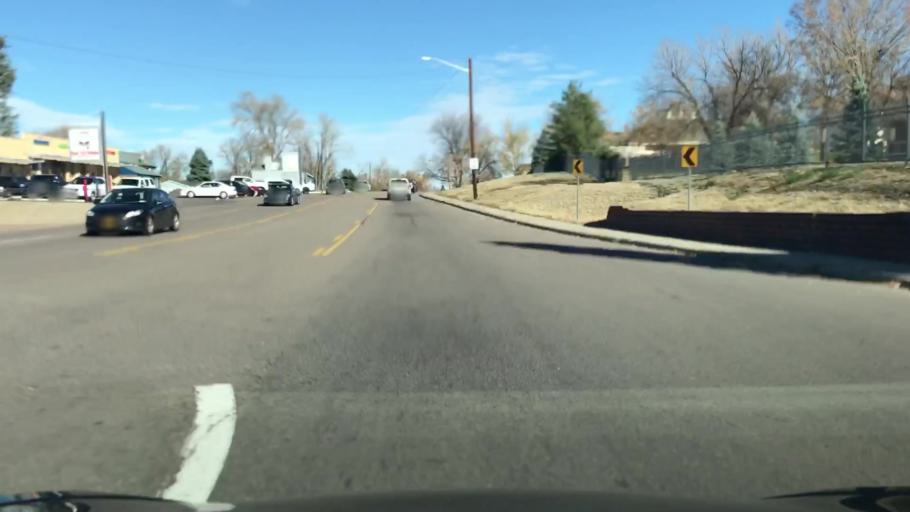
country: US
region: Colorado
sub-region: Arapahoe County
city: Glendale
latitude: 39.7269
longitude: -104.9034
